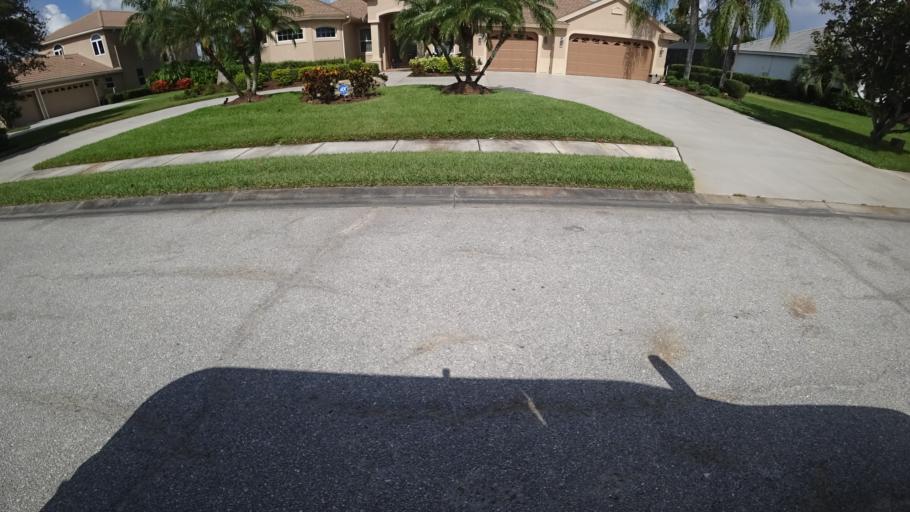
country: US
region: Florida
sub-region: Sarasota County
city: The Meadows
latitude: 27.4078
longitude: -82.4333
